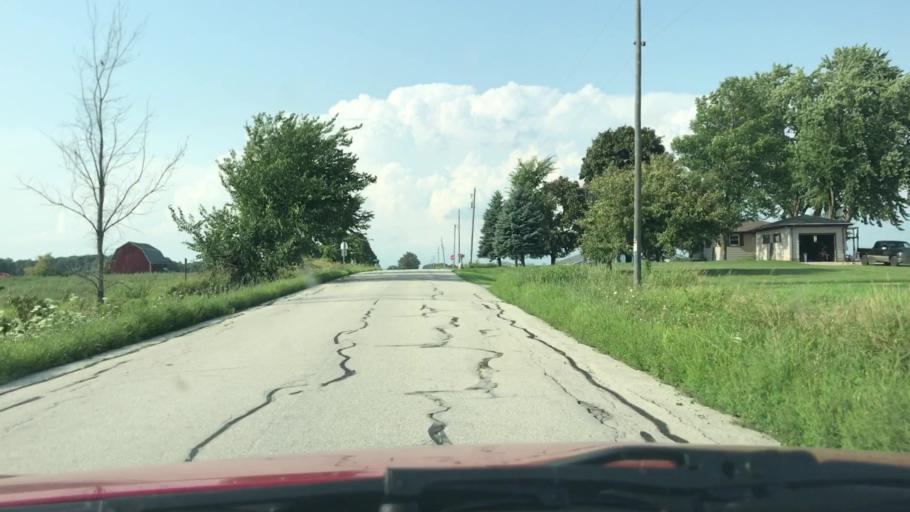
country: US
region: Wisconsin
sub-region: Brown County
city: Oneida
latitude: 44.4429
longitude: -88.1704
